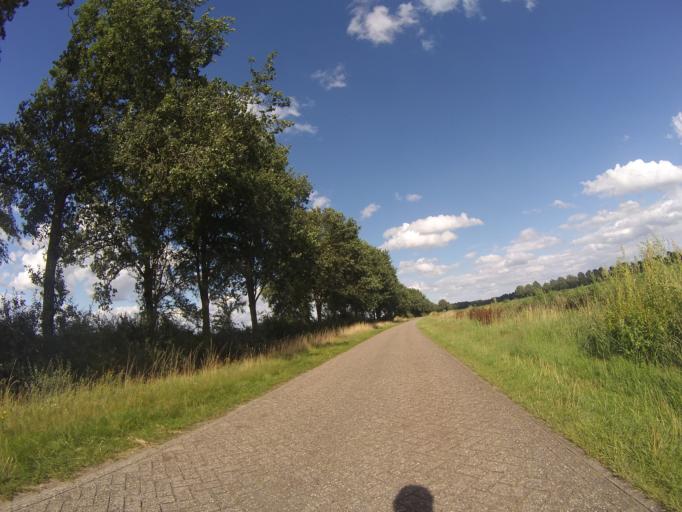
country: NL
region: Drenthe
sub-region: Gemeente Coevorden
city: Dalen
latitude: 52.7145
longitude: 6.8081
